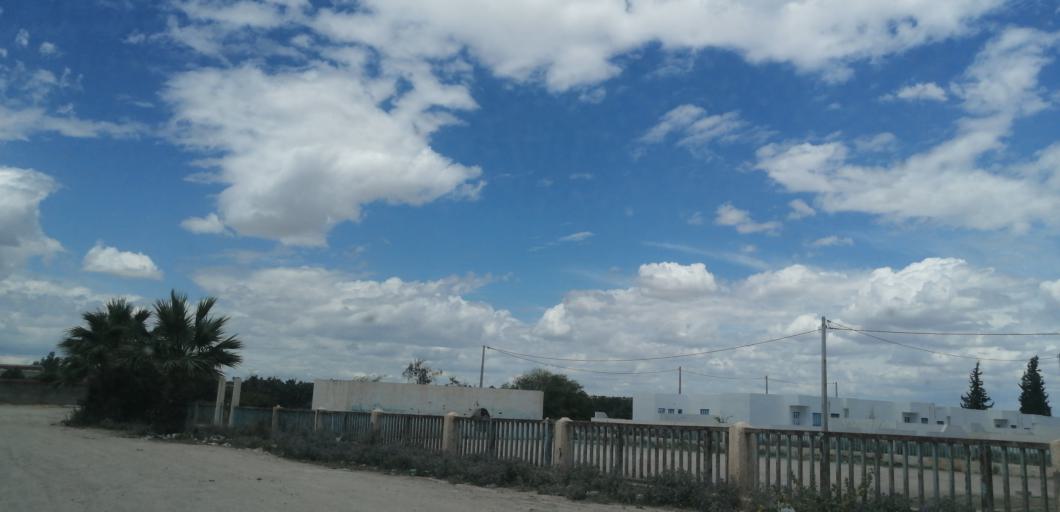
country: TN
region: Al Qayrawan
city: Kairouan
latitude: 35.6226
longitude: 9.9229
